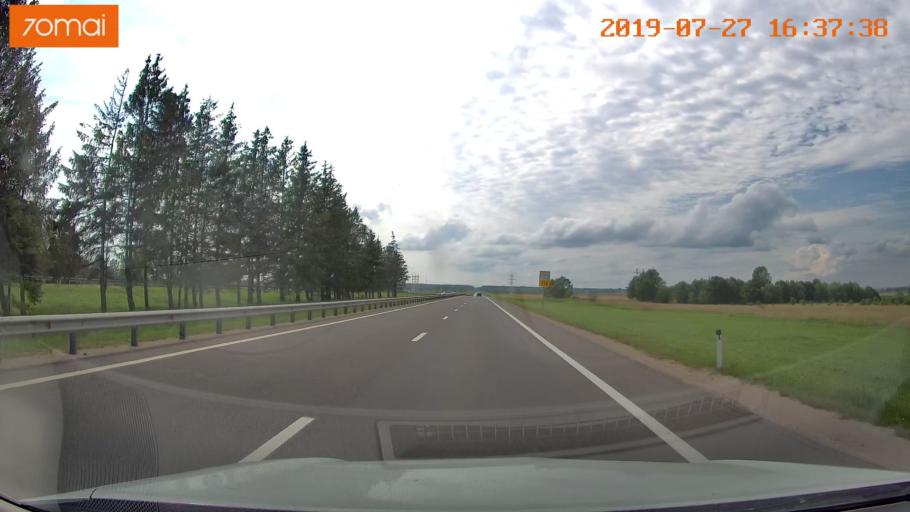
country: RU
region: Kaliningrad
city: Gvardeysk
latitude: 54.6487
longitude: 21.2503
